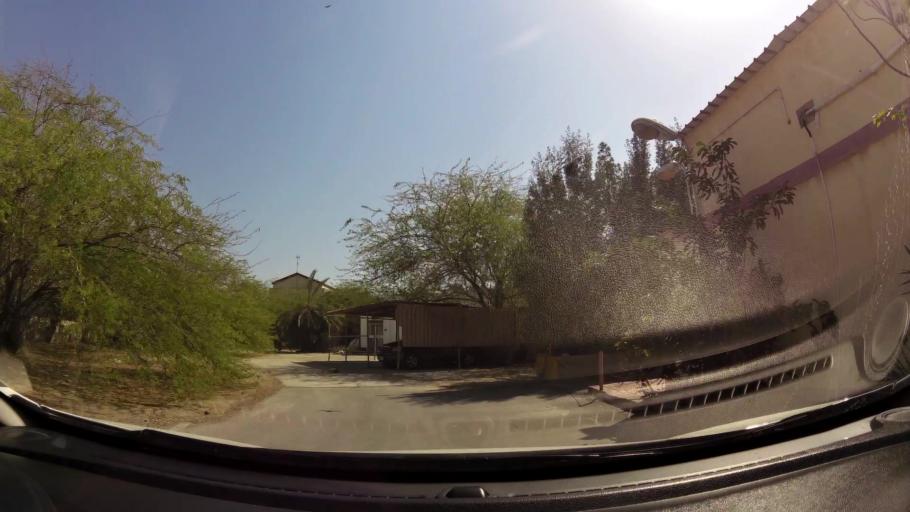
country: BH
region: Manama
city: Manama
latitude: 26.2093
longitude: 50.6065
